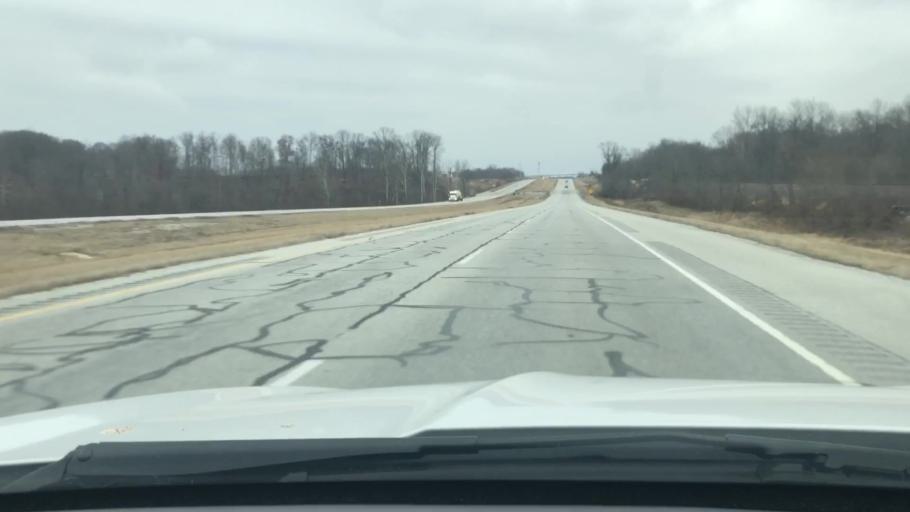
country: US
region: Indiana
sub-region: Cass County
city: Georgetown
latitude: 40.6502
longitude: -86.5588
